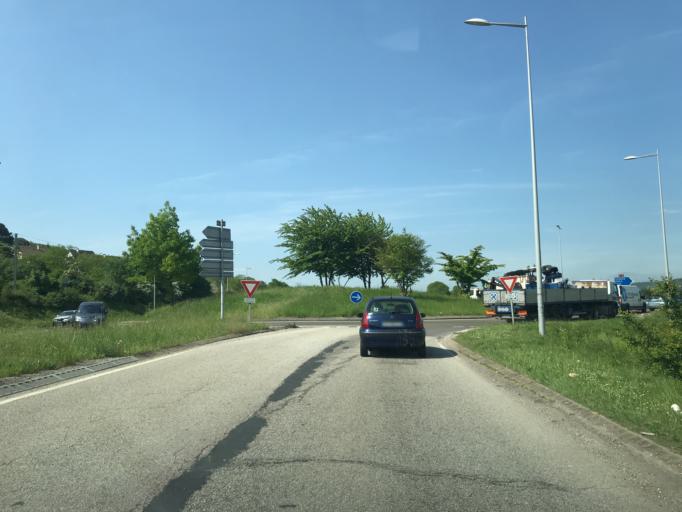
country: FR
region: Haute-Normandie
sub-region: Departement de la Seine-Maritime
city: Oissel
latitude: 49.3235
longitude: 1.0945
